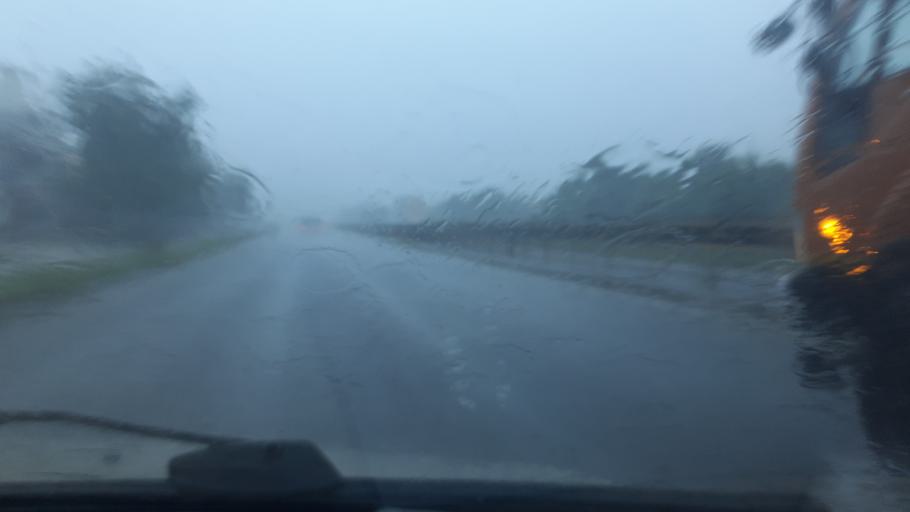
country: IN
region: Tamil Nadu
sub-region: Virudhunagar
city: Tiruttangal
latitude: 9.4637
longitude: 77.9336
